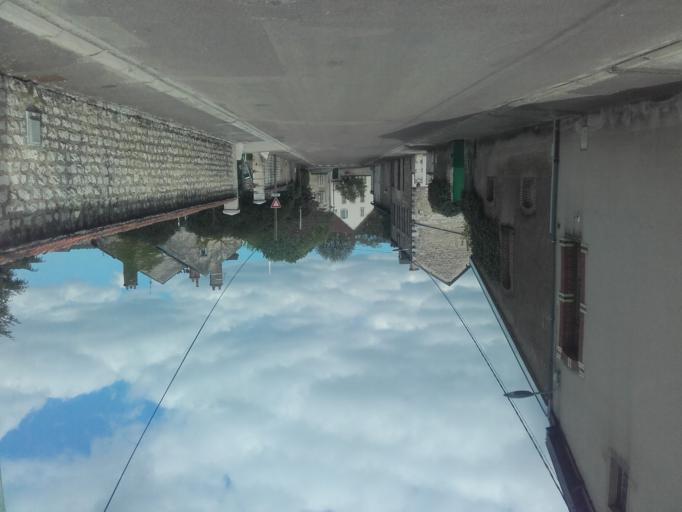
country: FR
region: Bourgogne
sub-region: Departement de la Cote-d'Or
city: Nuits-Saint-Georges
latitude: 47.1325
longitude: 4.9531
